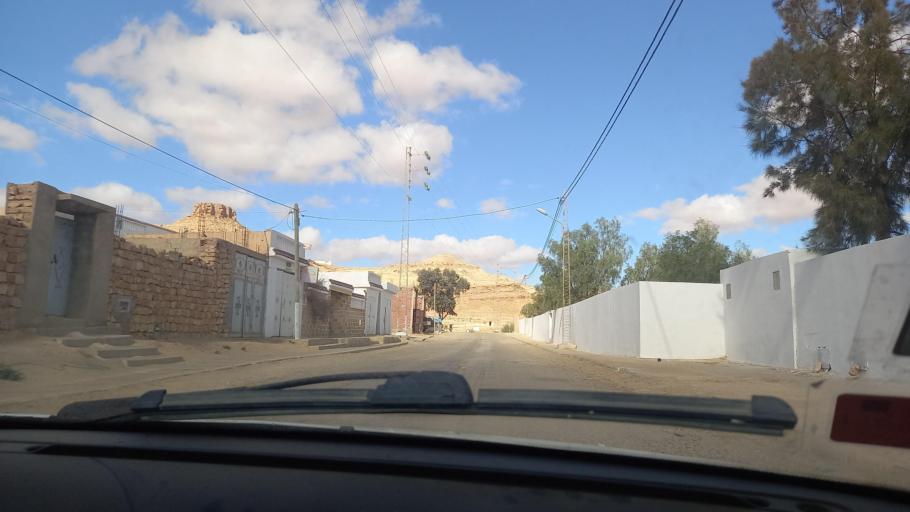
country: TN
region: Tataouine
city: Tataouine
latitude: 32.9832
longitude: 10.2620
